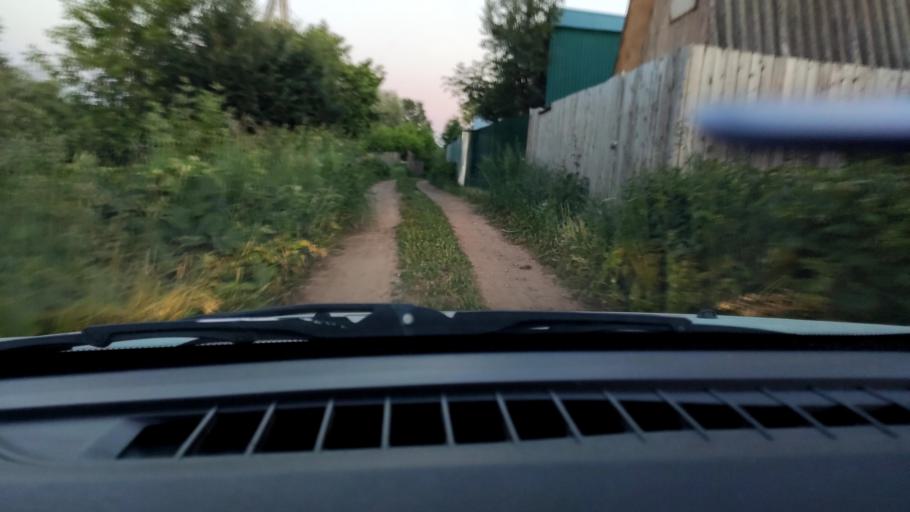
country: RU
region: Perm
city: Kondratovo
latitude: 57.9525
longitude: 56.1449
